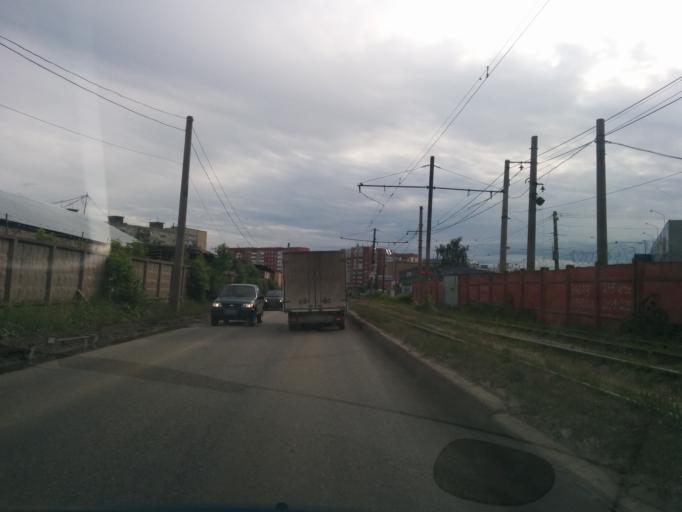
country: RU
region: Perm
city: Kondratovo
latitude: 58.0019
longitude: 56.1501
